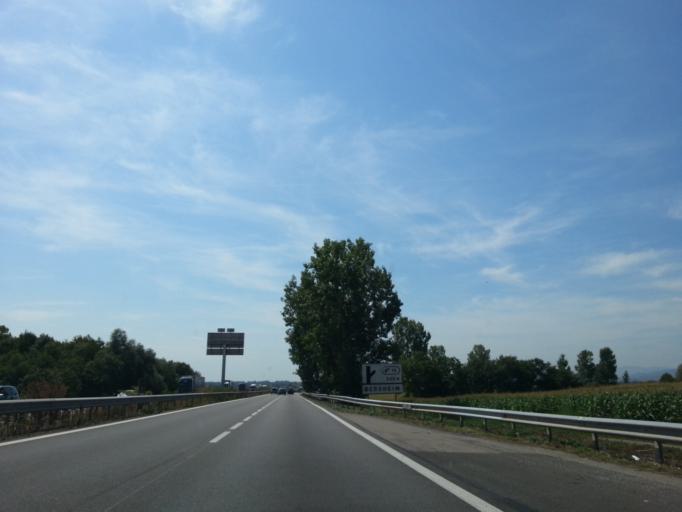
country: FR
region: Alsace
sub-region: Departement du Haut-Rhin
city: Guemar
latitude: 48.2109
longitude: 7.4015
